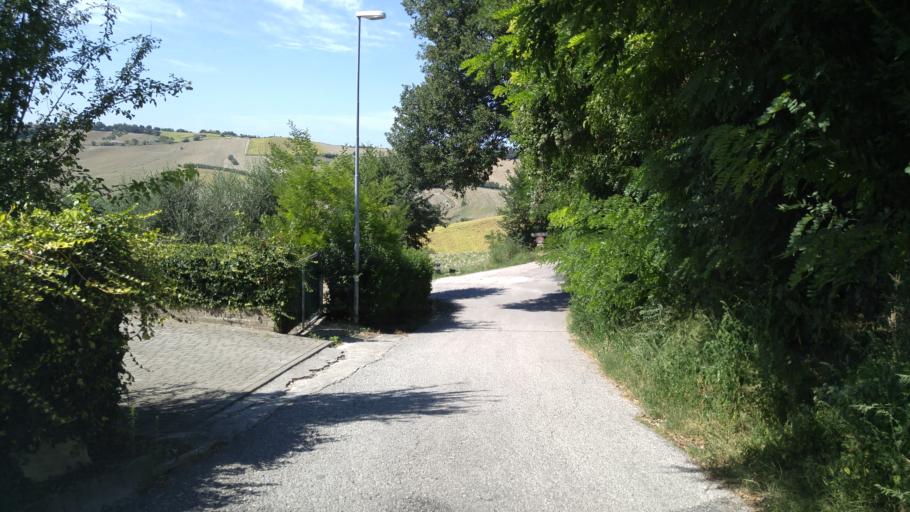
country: IT
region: The Marches
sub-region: Provincia di Pesaro e Urbino
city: San Giorgio di Pesaro
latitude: 43.7171
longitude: 12.9747
